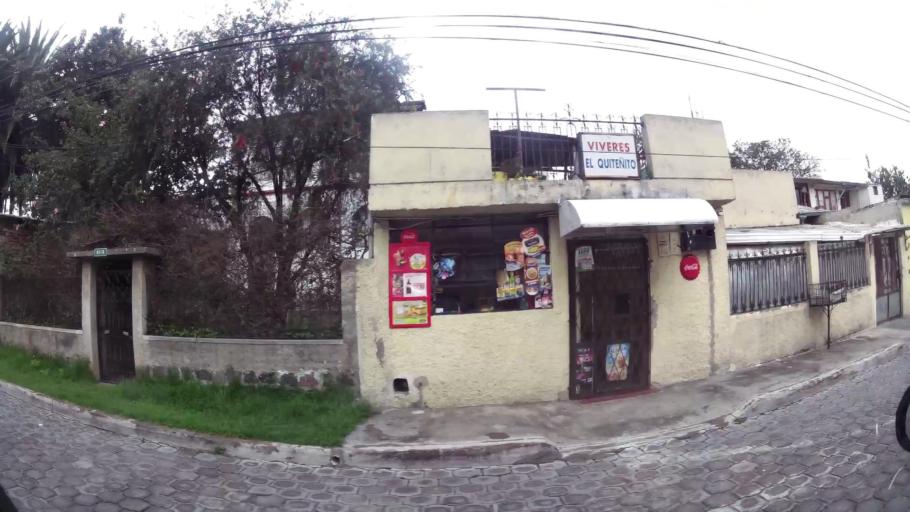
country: EC
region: Pichincha
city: Sangolqui
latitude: -0.2968
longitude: -78.4697
